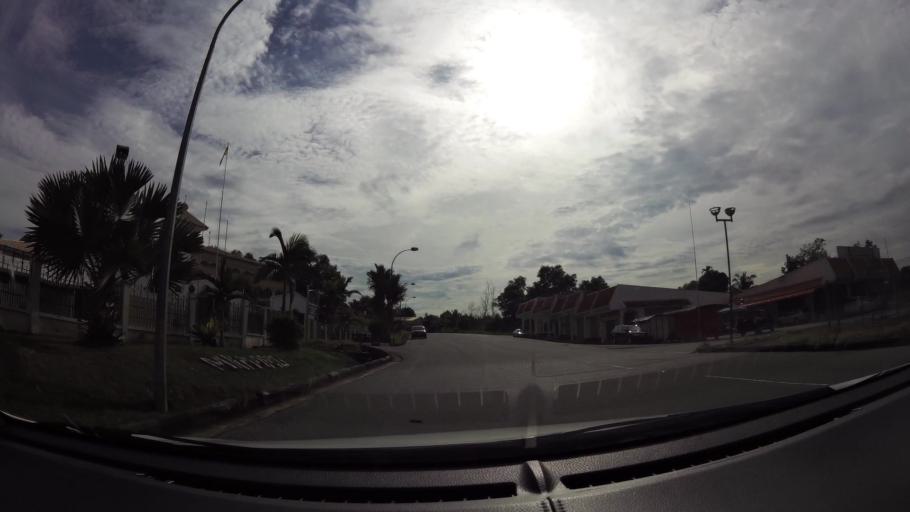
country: BN
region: Brunei and Muara
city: Bandar Seri Begawan
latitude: 4.9008
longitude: 114.8883
